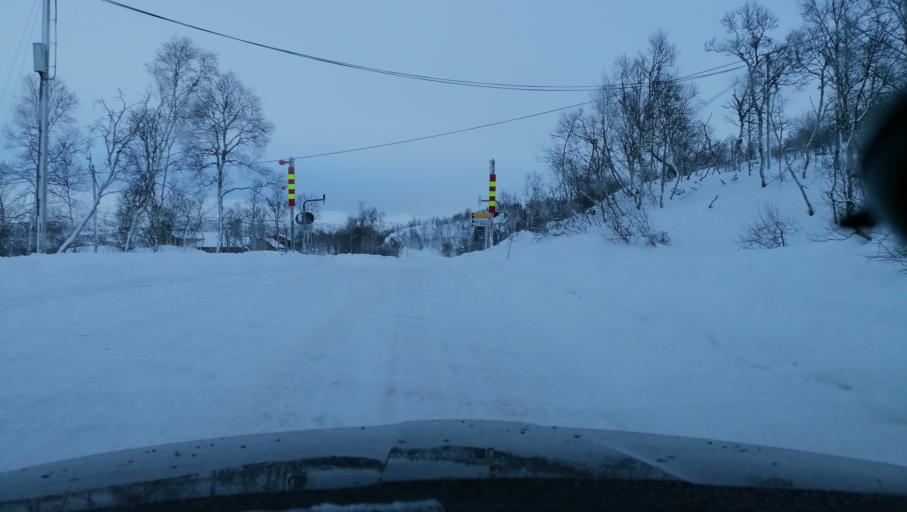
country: NO
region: Aust-Agder
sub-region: Bykle
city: Hovden
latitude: 59.6402
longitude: 7.4548
